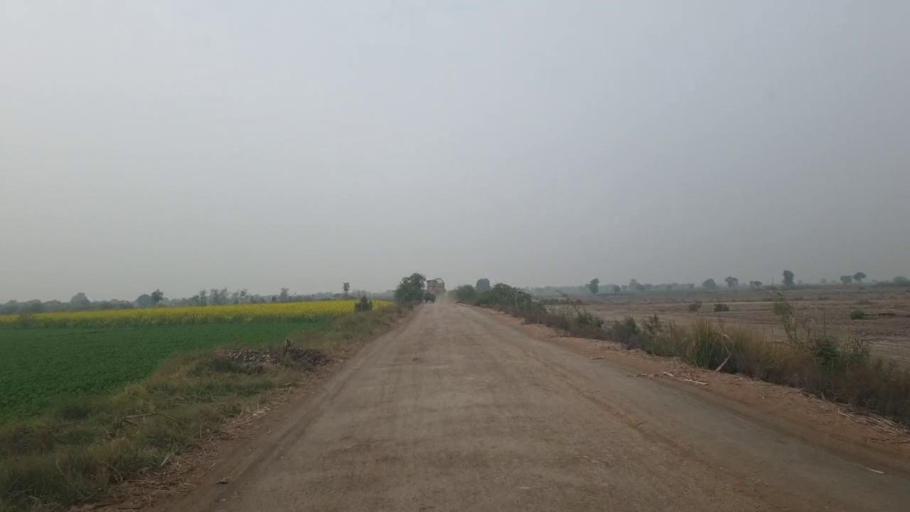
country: PK
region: Sindh
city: Tando Adam
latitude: 25.8073
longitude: 68.7201
